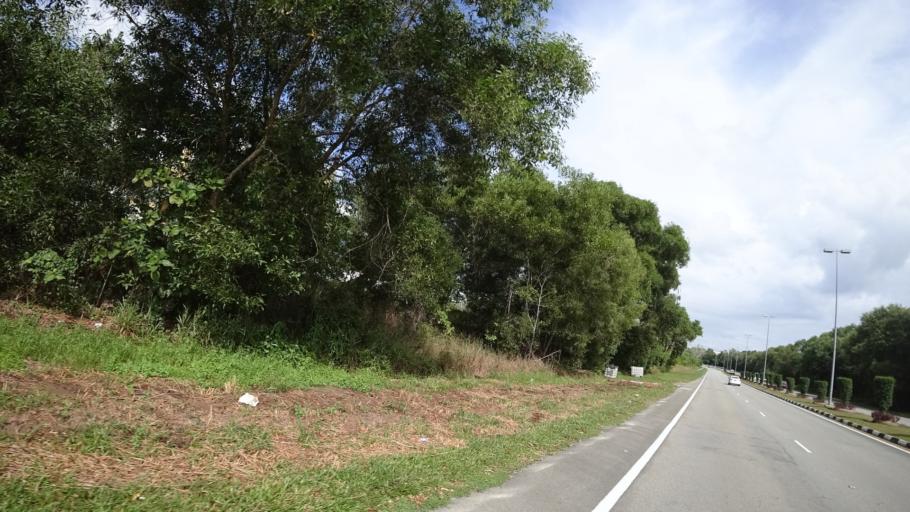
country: BN
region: Tutong
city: Tutong
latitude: 4.8117
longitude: 114.6551
